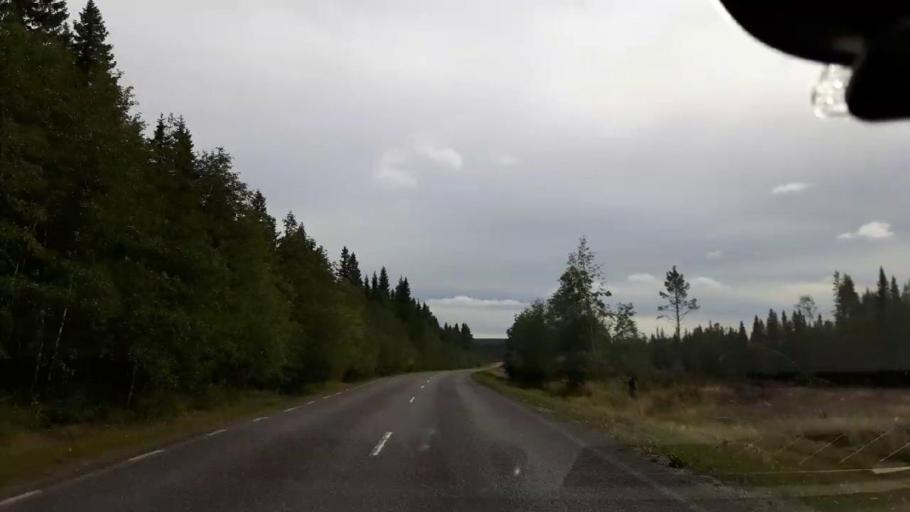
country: SE
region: Jaemtland
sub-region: Ragunda Kommun
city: Hammarstrand
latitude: 63.1326
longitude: 15.8809
